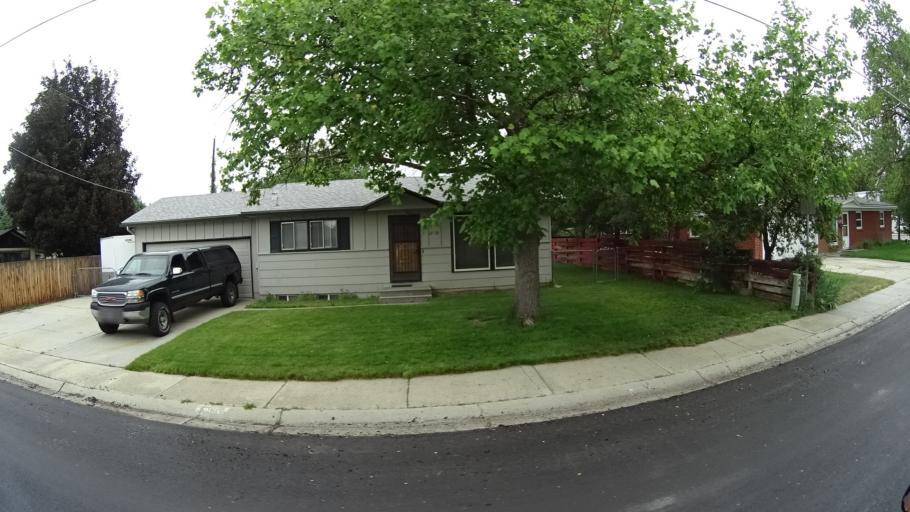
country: US
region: Idaho
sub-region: Ada County
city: Boise
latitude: 43.5758
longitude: -116.2037
